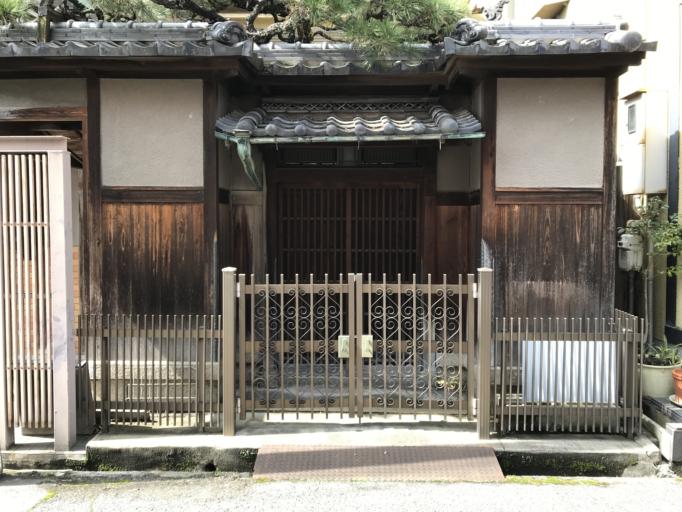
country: JP
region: Nara
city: Nara-shi
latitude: 34.6456
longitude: 135.7819
